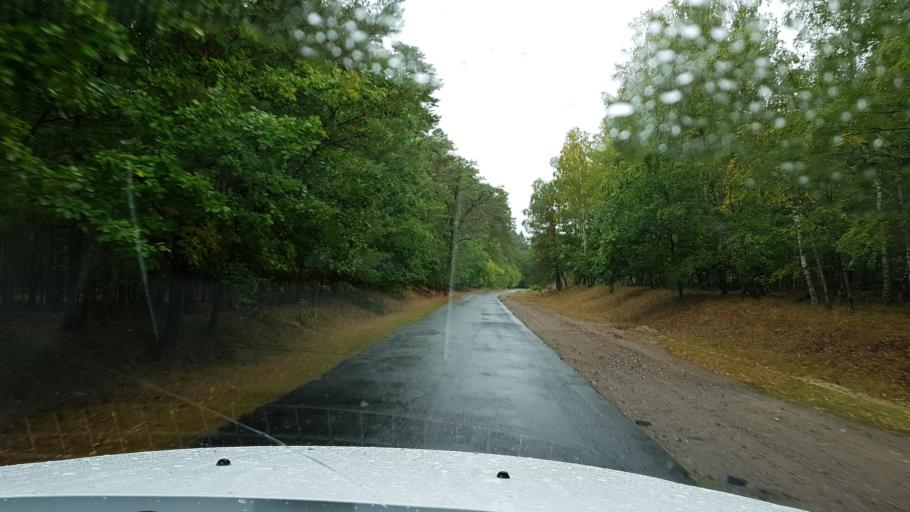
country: PL
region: West Pomeranian Voivodeship
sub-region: Powiat gryfinski
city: Cedynia
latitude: 52.9561
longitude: 14.2000
